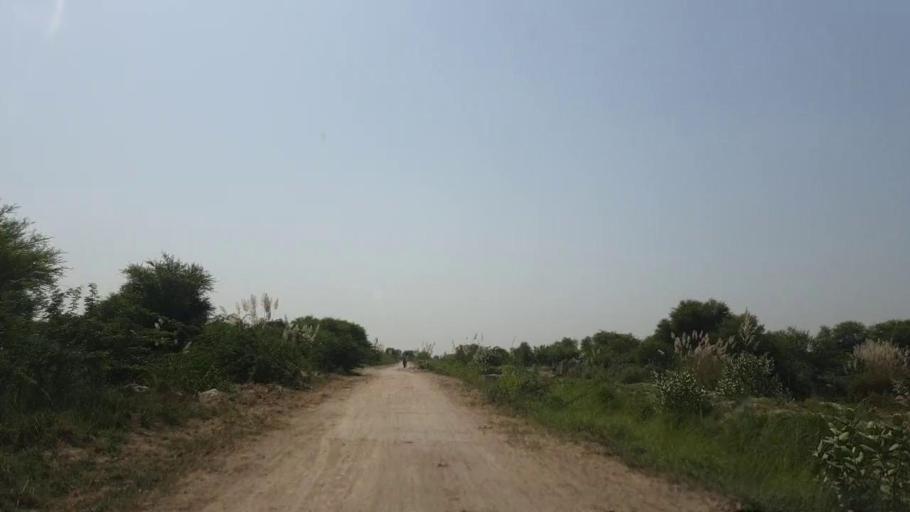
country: PK
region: Sindh
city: Jhol
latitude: 25.8577
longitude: 69.0302
